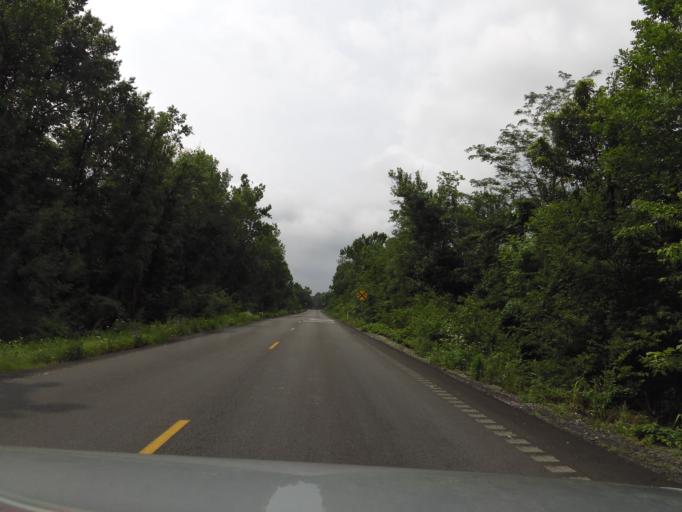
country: US
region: Kentucky
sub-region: Hopkins County
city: Madisonville
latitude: 37.3112
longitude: -87.3681
